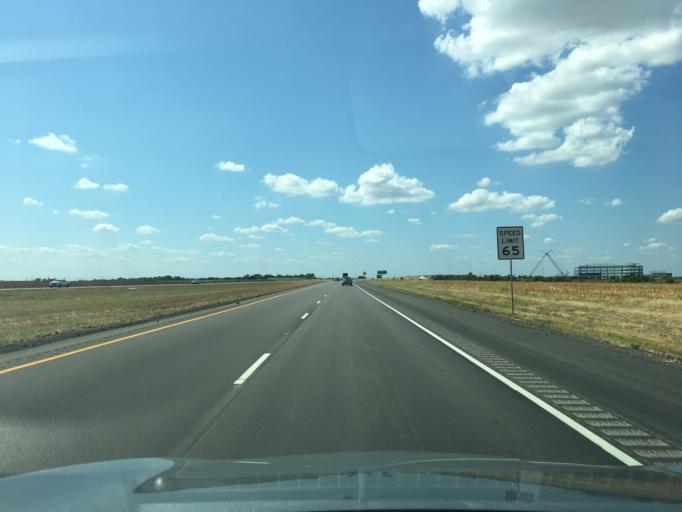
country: US
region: Texas
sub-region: Tarrant County
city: Mansfield
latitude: 32.5292
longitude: -97.0941
